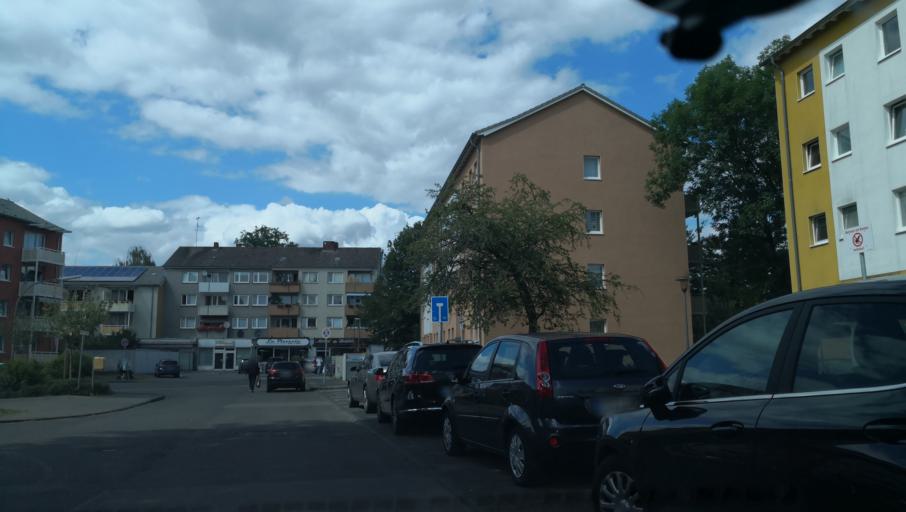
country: DE
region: North Rhine-Westphalia
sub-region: Regierungsbezirk Koln
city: Mengenich
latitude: 50.9663
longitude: 6.8865
